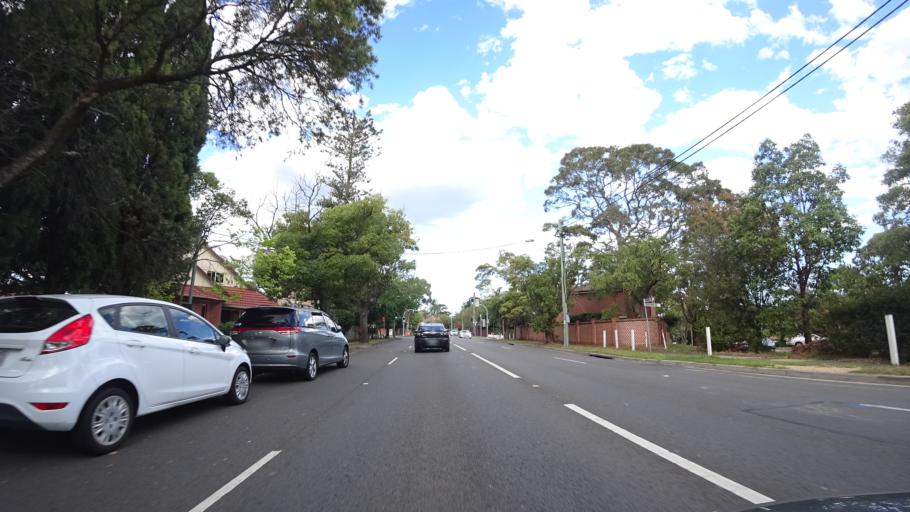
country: AU
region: New South Wales
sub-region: Willoughby
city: Chatswood
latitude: -33.8022
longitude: 151.1857
